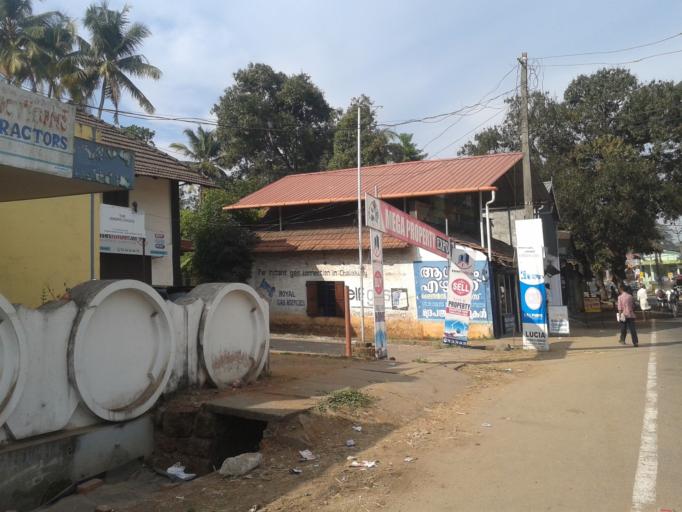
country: IN
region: Kerala
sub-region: Thrissur District
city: Kizhake Chalakudi
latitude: 10.3077
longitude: 76.3366
